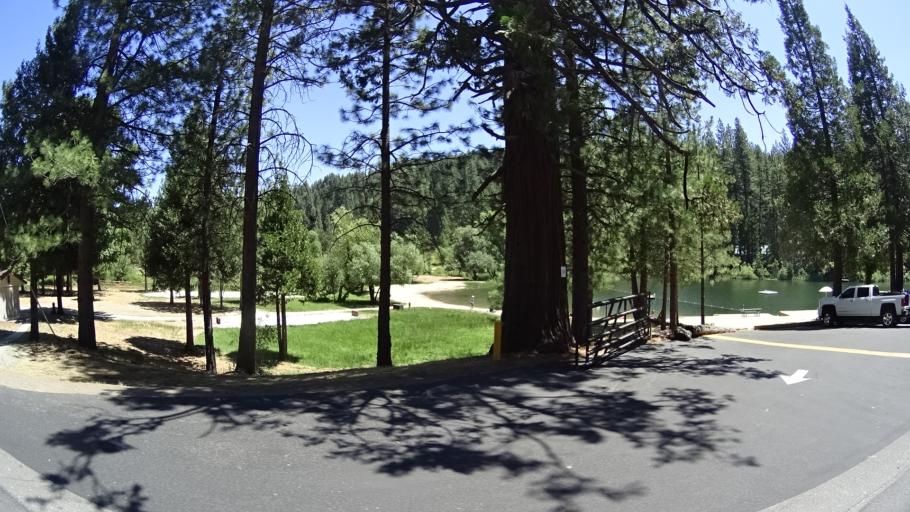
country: US
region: California
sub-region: Calaveras County
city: Arnold
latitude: 38.2468
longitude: -120.3353
